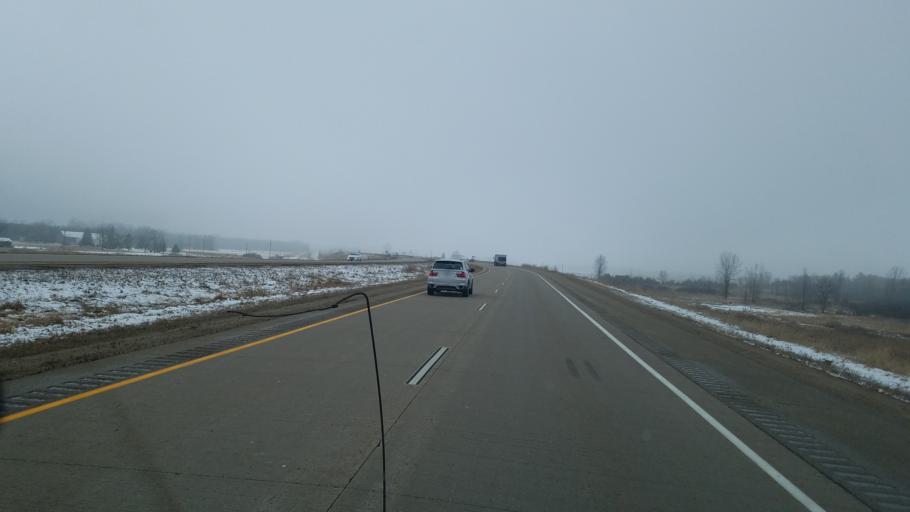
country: US
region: Wisconsin
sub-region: Winnebago County
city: Winneconne
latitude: 44.2220
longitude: -88.7018
